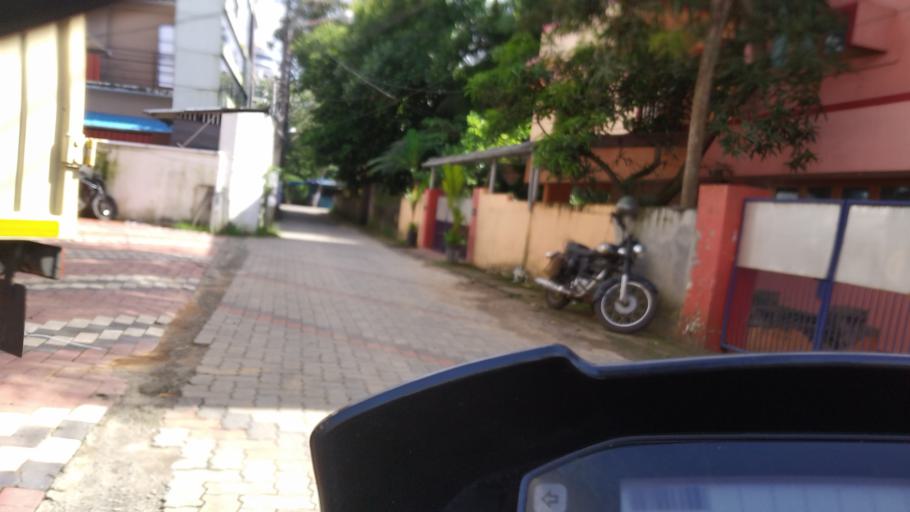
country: IN
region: Kerala
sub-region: Ernakulam
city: Cochin
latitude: 9.9961
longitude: 76.2890
